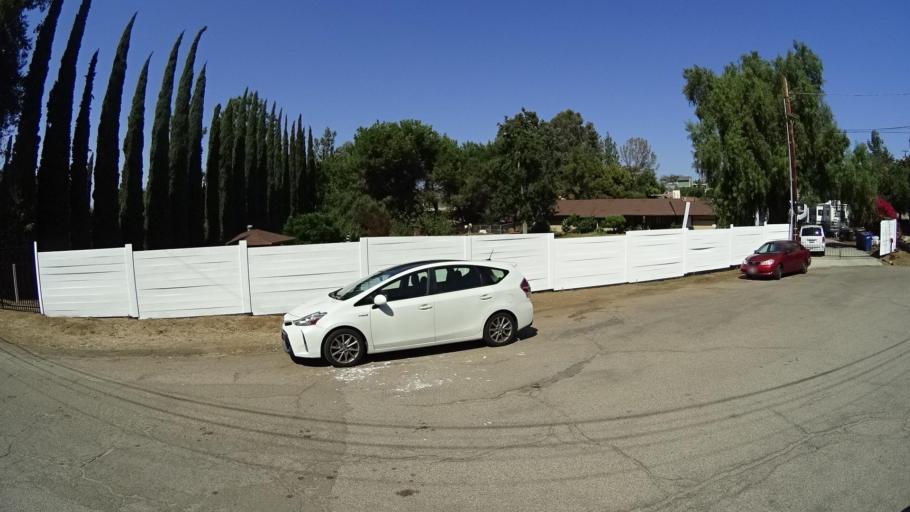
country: US
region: California
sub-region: San Diego County
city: Granite Hills
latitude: 32.7834
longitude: -116.9149
